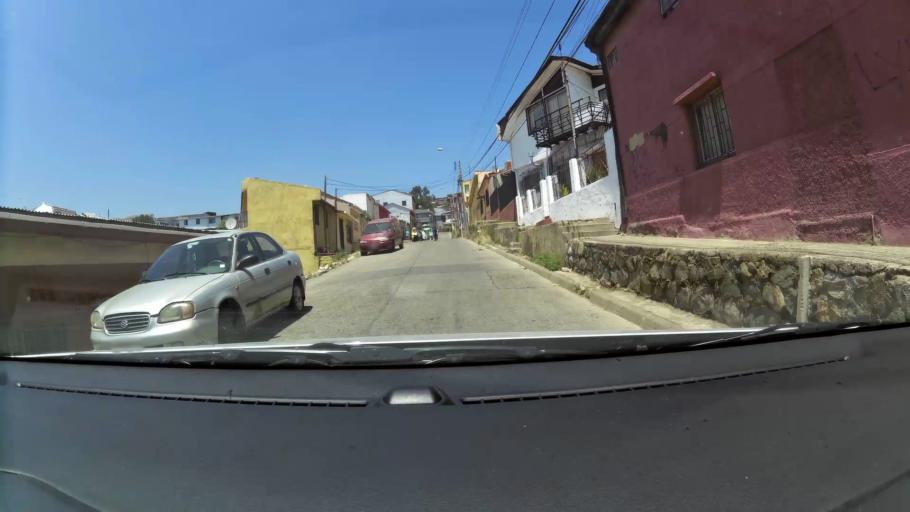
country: CL
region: Valparaiso
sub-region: Provincia de Valparaiso
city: Valparaiso
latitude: -33.0312
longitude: -71.6417
